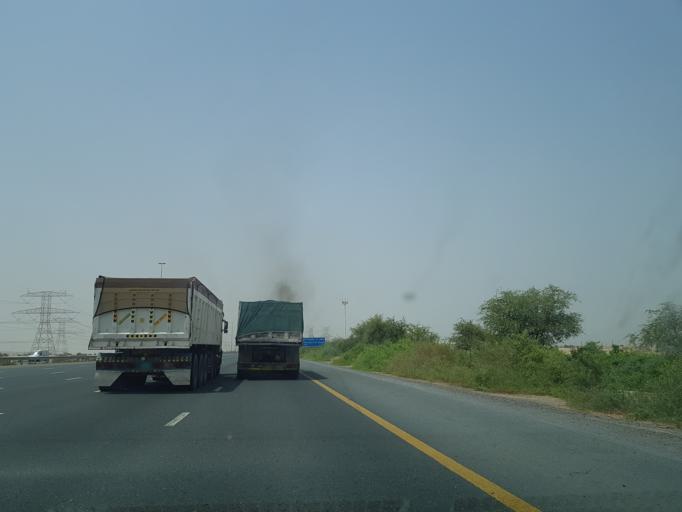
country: AE
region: Dubai
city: Dubai
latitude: 25.0423
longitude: 55.3014
